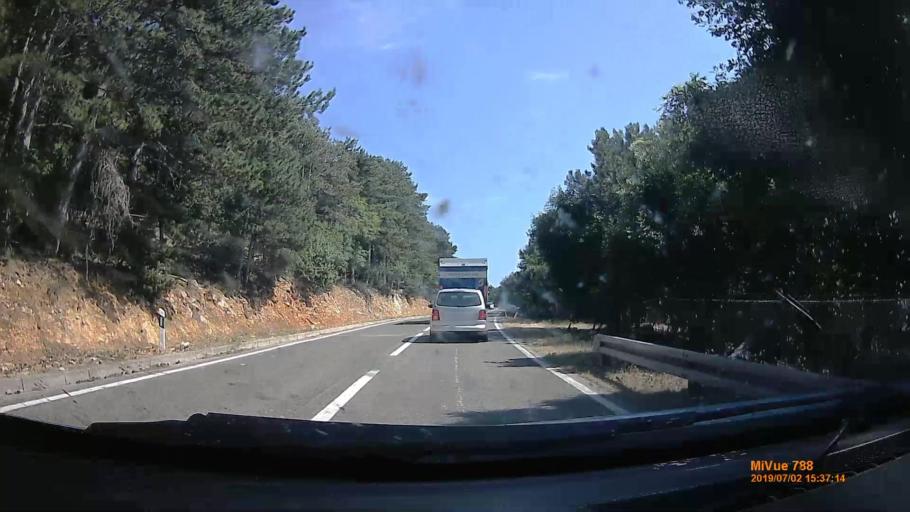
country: HR
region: Primorsko-Goranska
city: Cres
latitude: 44.9800
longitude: 14.4150
